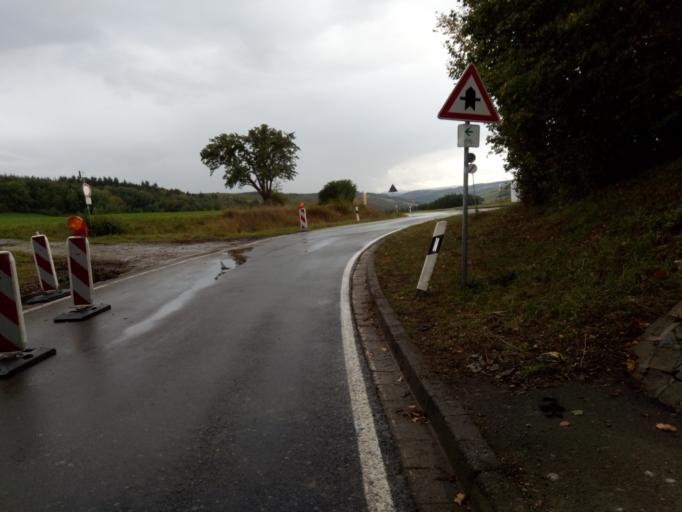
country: DE
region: Rheinland-Pfalz
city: Daubach
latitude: 49.8430
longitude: 7.6318
